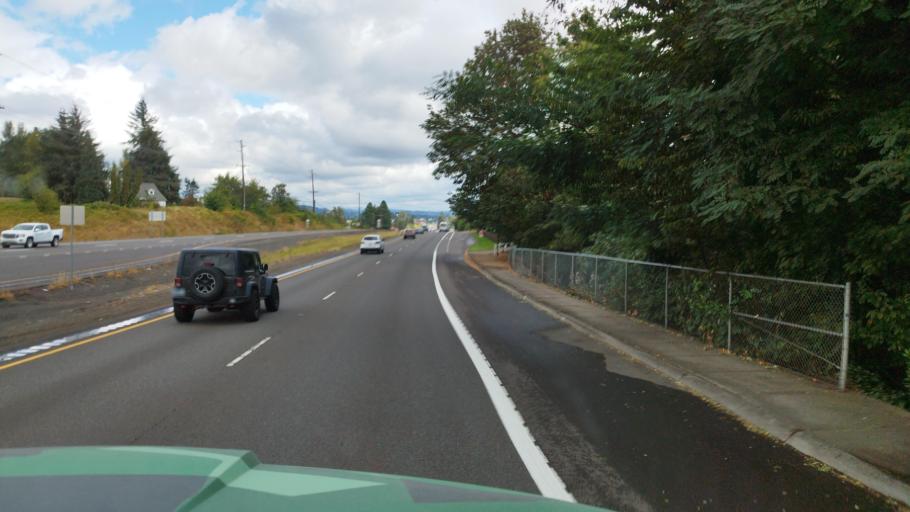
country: US
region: Oregon
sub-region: Washington County
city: Sherwood
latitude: 45.3540
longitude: -122.8666
